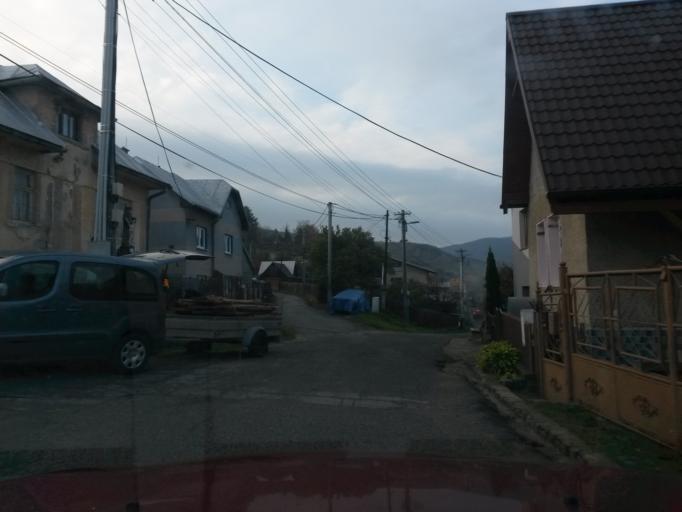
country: SK
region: Kosicky
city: Kosice
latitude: 48.7764
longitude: 21.2036
